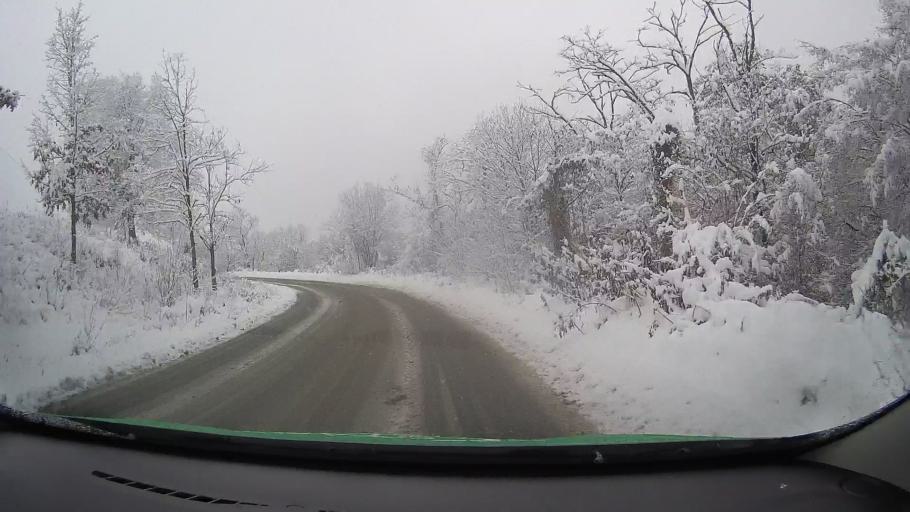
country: RO
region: Hunedoara
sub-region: Comuna Teliucu Inferior
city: Teliucu Inferior
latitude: 45.7047
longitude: 22.8816
